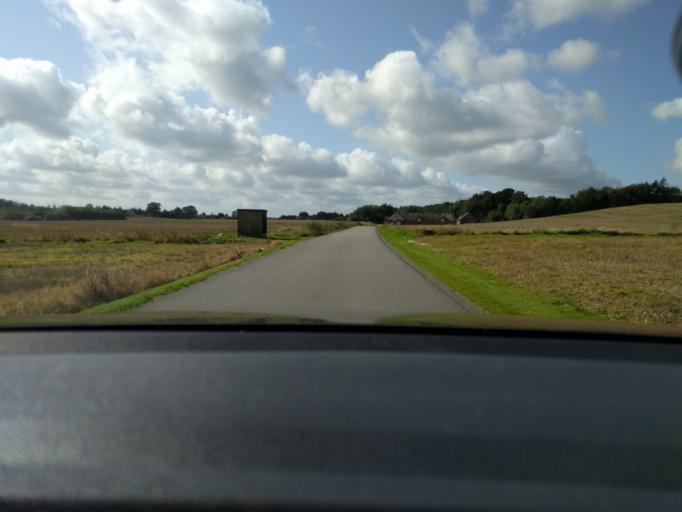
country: DK
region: Central Jutland
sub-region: Silkeborg Kommune
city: Silkeborg
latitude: 56.2658
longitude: 9.5602
